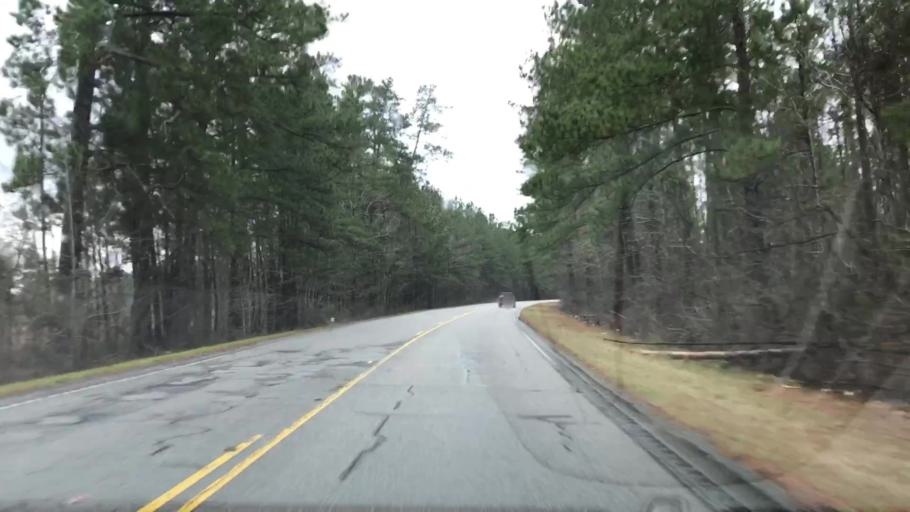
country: US
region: South Carolina
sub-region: Williamsburg County
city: Andrews
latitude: 33.5207
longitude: -79.4931
